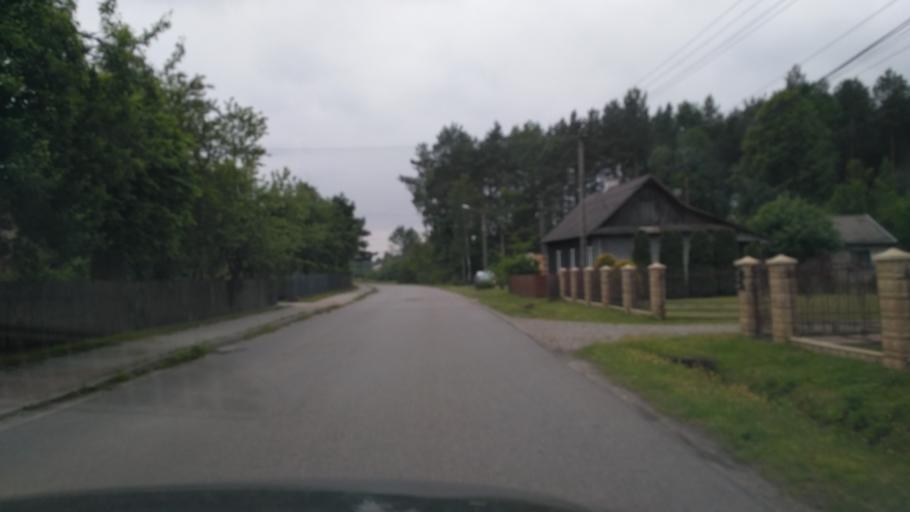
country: PL
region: Subcarpathian Voivodeship
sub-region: Powiat kolbuszowski
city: Niwiska
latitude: 50.1533
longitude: 21.6707
